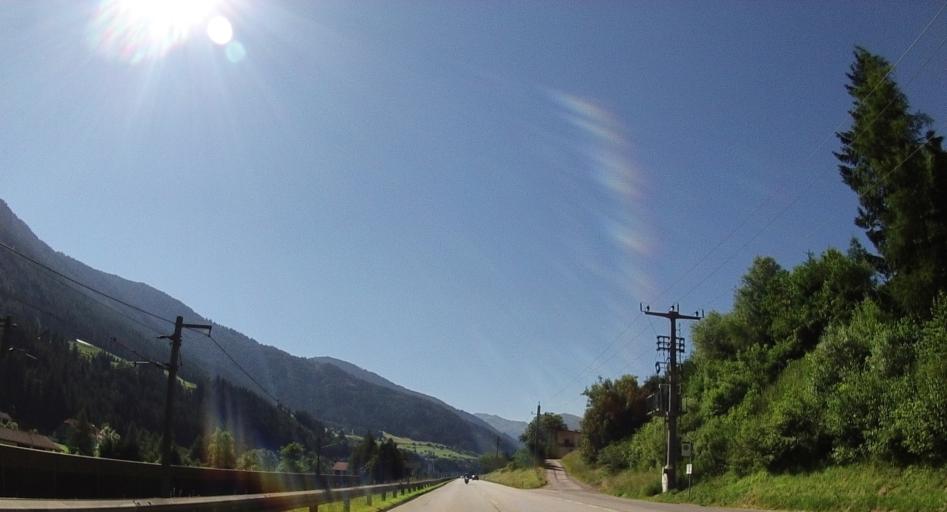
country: AT
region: Tyrol
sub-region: Politischer Bezirk Innsbruck Land
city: Steinach am Brenner
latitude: 47.1071
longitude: 11.4569
